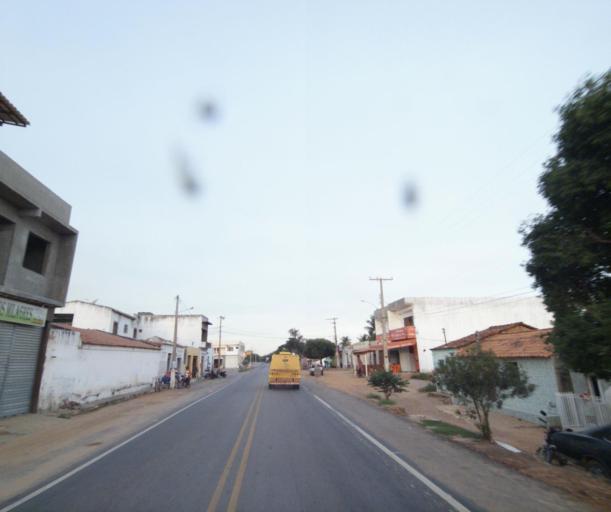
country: BR
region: Bahia
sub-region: Brumado
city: Brumado
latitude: -14.2473
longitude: -41.7316
